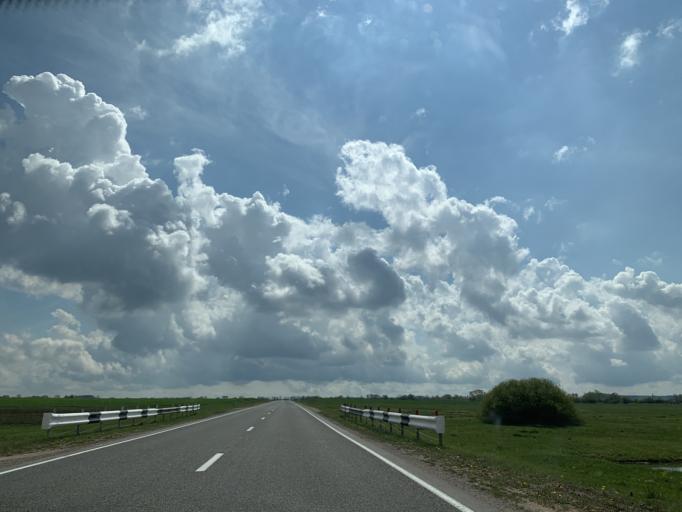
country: BY
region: Minsk
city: Nyasvizh
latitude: 53.2404
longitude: 26.7099
